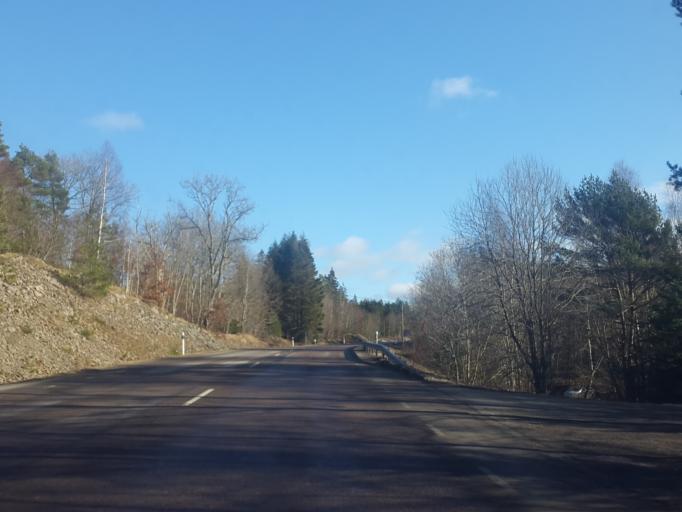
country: SE
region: Vaestra Goetaland
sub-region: Alingsas Kommun
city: Alingsas
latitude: 57.9534
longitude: 12.4739
